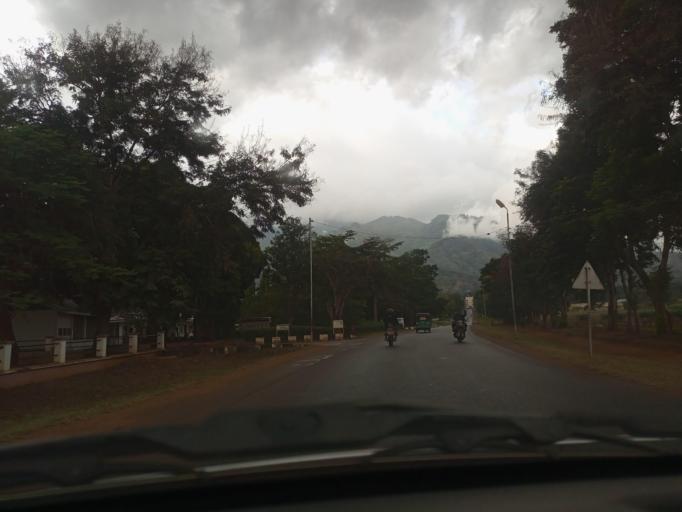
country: TZ
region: Morogoro
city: Morogoro
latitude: -6.8444
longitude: 37.6577
